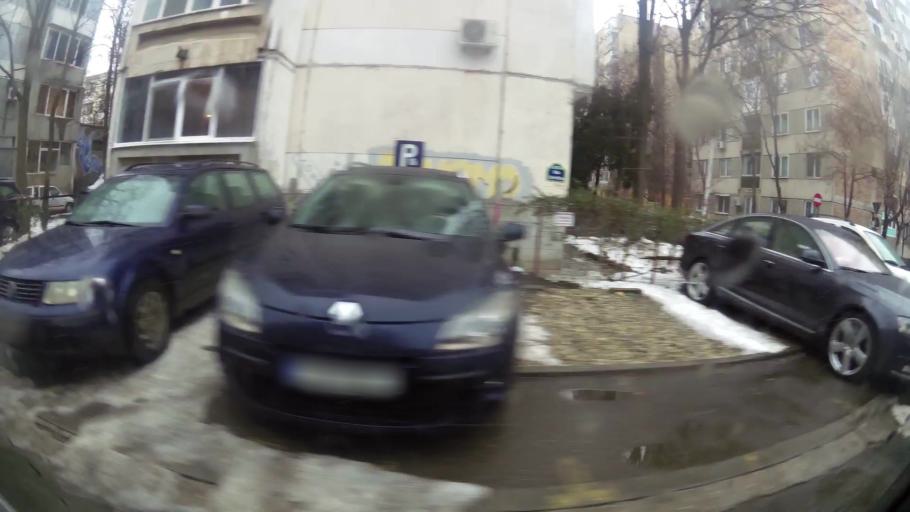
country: RO
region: Ilfov
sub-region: Comuna Chiajna
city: Rosu
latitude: 44.4318
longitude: 26.0113
